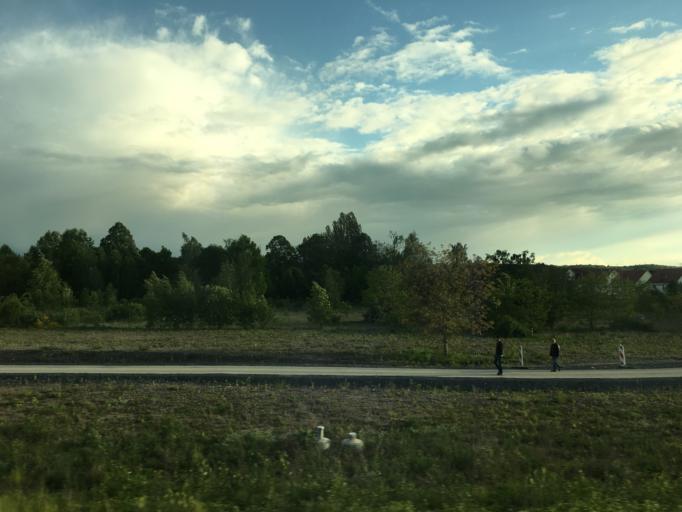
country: DE
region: Saxony
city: Coswig
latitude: 51.1107
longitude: 13.6183
